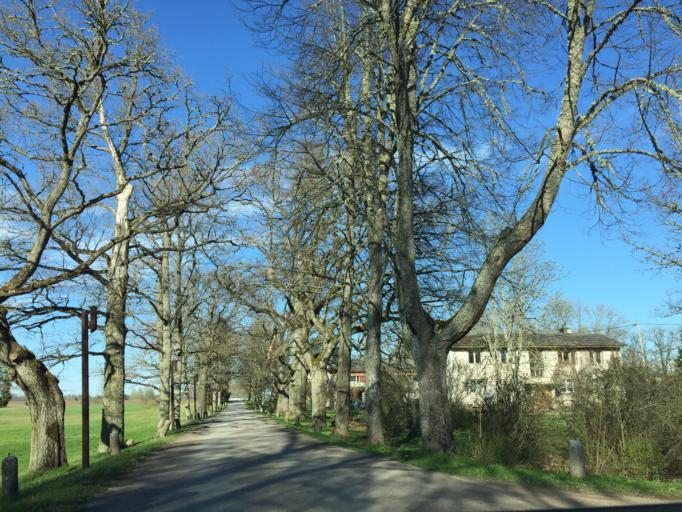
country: EE
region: Vorumaa
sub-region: Antsla vald
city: Vana-Antsla
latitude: 57.9025
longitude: 26.2820
